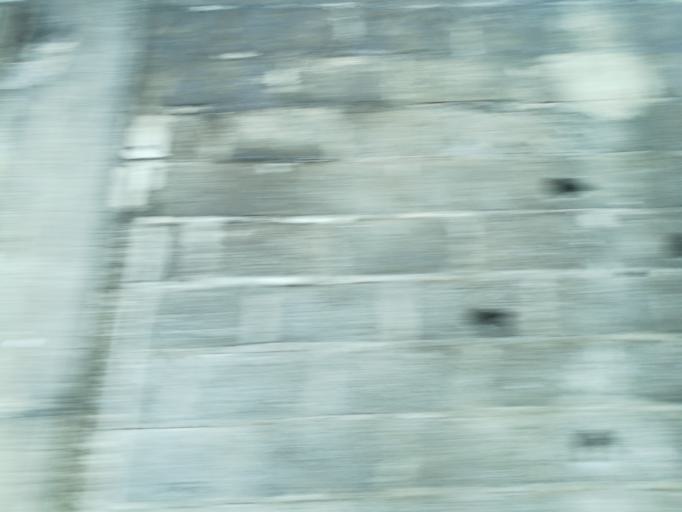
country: NG
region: Rivers
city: Port Harcourt
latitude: 4.8149
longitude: 7.0694
